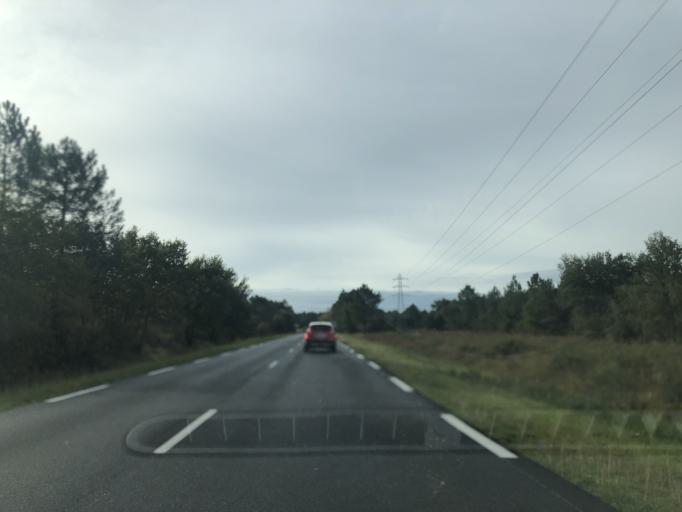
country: FR
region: Aquitaine
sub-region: Departement de la Gironde
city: Martignas-sur-Jalle
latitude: 44.7967
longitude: -0.8717
